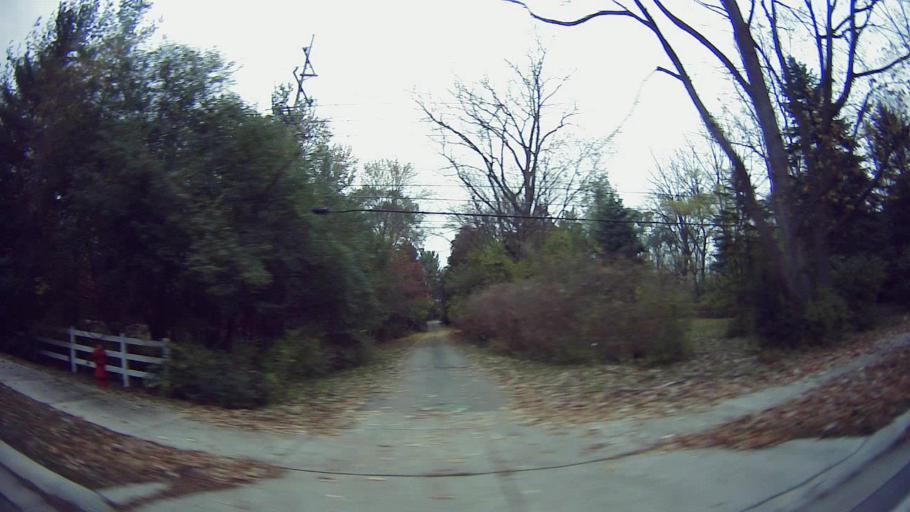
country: US
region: Michigan
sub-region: Oakland County
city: Bingham Farms
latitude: 42.5308
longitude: -83.2530
